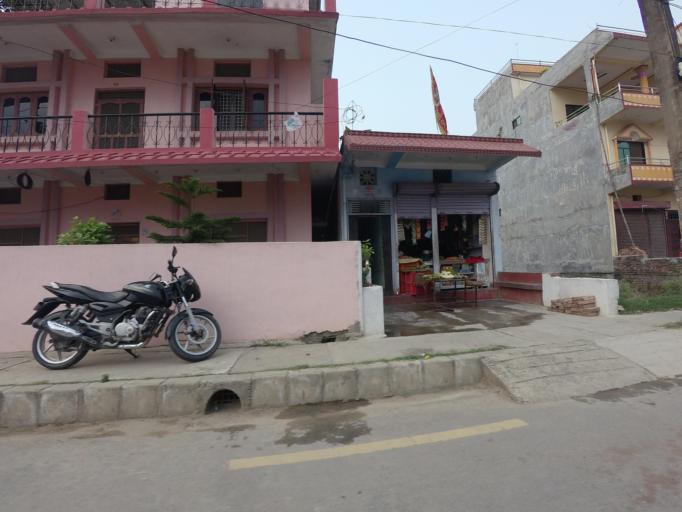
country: NP
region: Western Region
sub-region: Lumbini Zone
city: Bhairahawa
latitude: 27.5198
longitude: 83.4436
